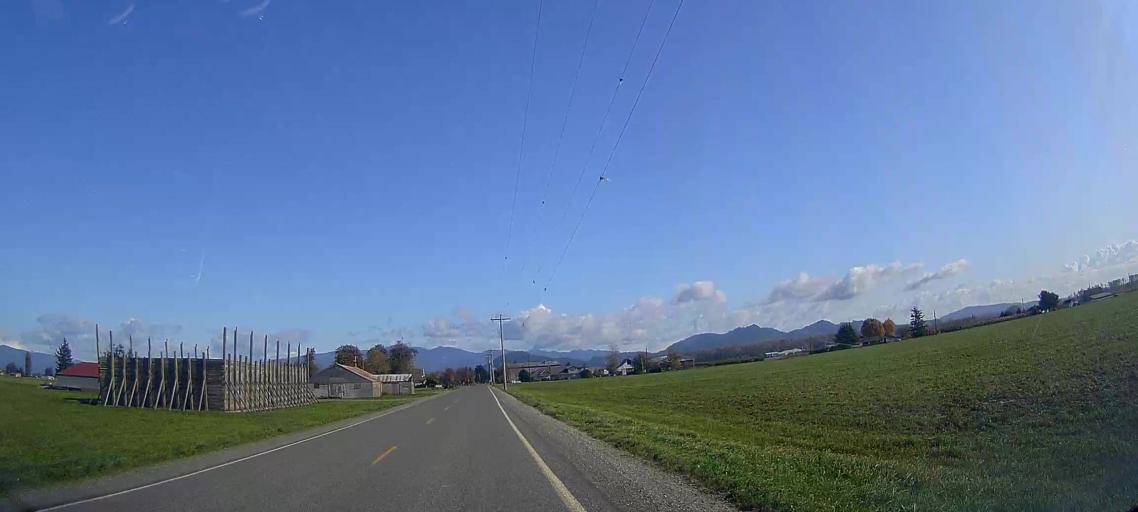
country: US
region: Washington
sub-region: Skagit County
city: Mount Vernon
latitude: 48.3993
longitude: -122.4044
